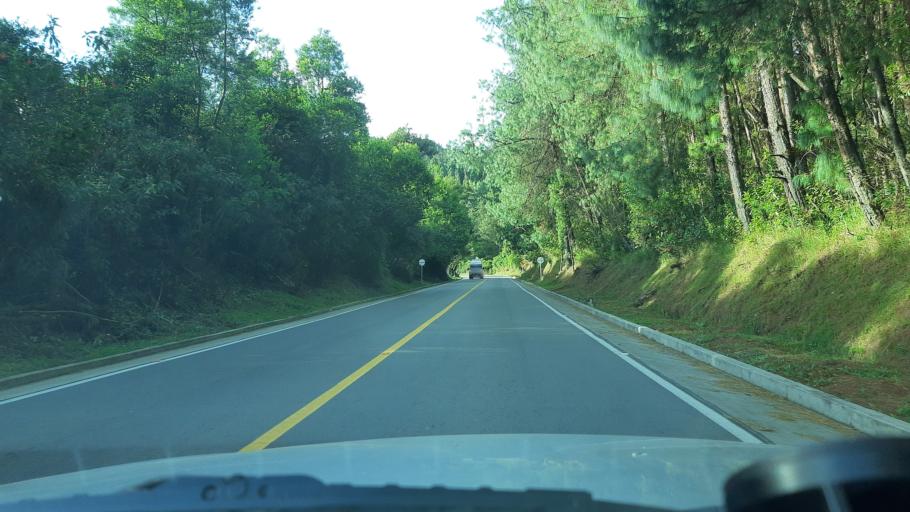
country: CO
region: Cundinamarca
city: Choconta
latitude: 5.0976
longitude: -73.6608
